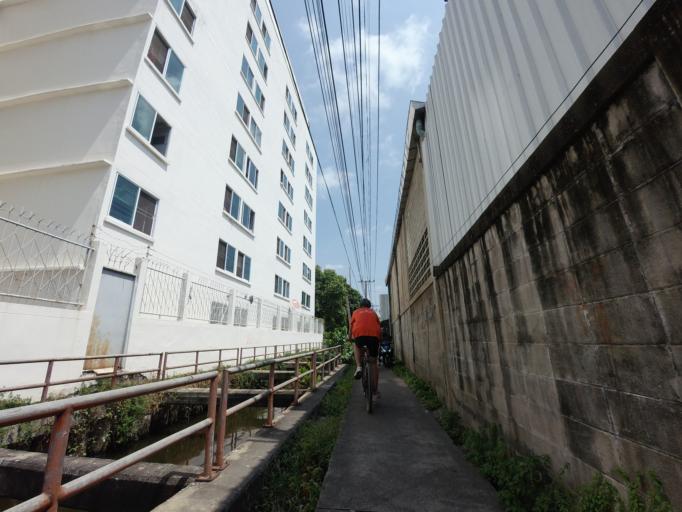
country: TH
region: Bangkok
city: Chom Thong
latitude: 13.6534
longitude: 100.4962
